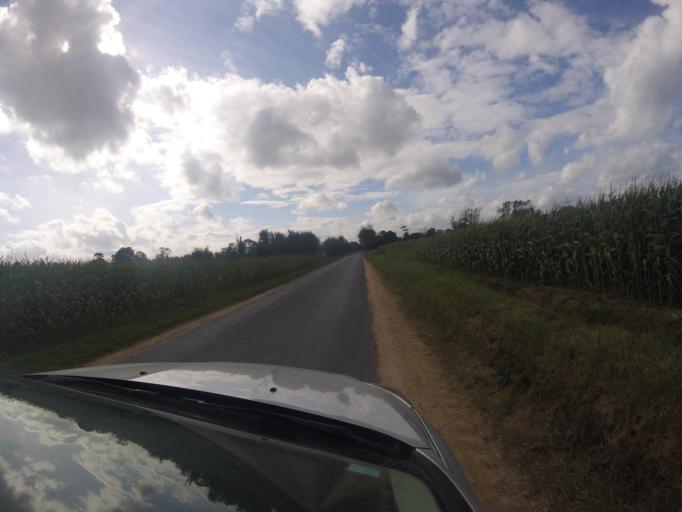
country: FR
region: Lower Normandy
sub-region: Departement du Calvados
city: Saint-Vigor-le-Grand
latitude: 49.3293
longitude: -0.6584
